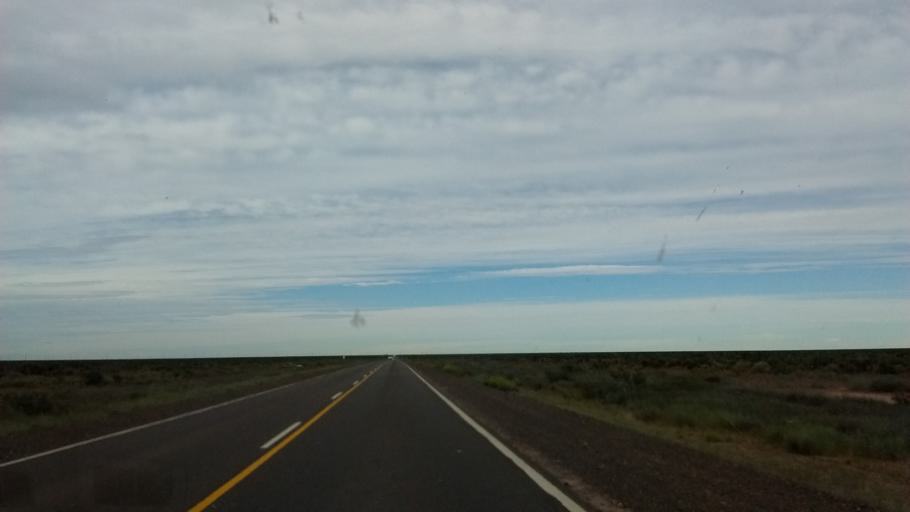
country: AR
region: Rio Negro
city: Contraalmirante Cordero
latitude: -38.4979
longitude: -68.0626
